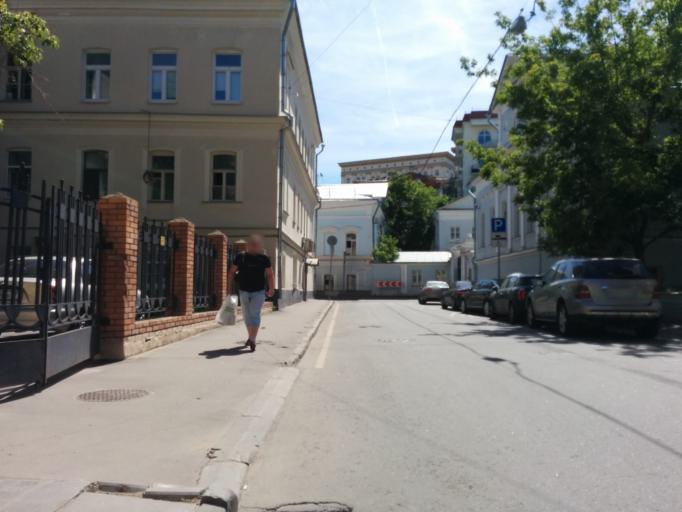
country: RU
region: Moscow
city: Moscow
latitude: 55.7423
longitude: 37.6222
